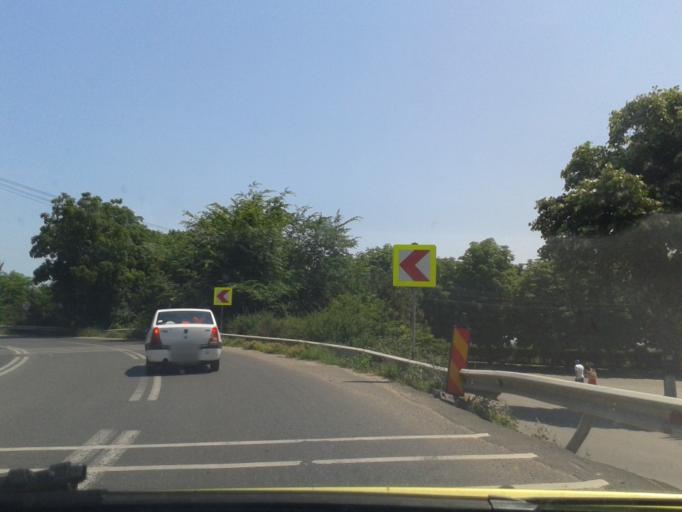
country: RO
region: Constanta
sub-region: Oras Eforie
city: Eforie Nord
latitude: 44.0586
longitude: 28.6320
